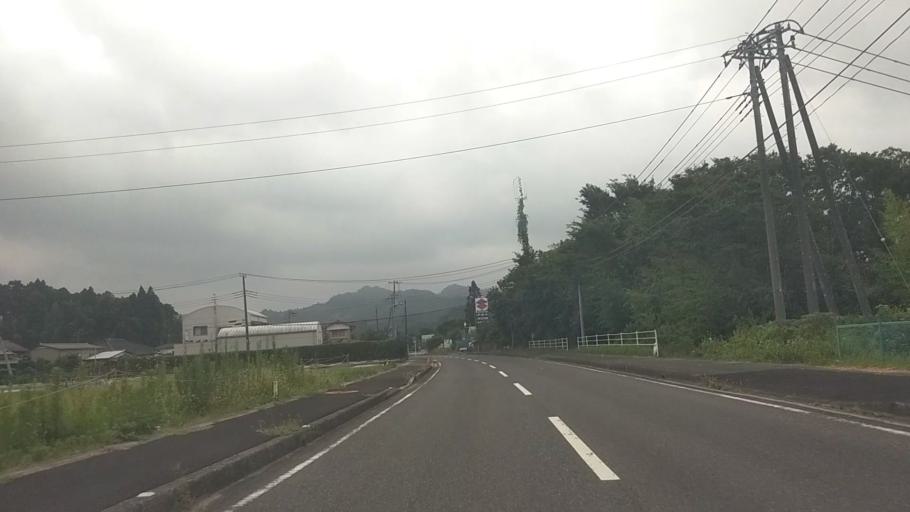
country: JP
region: Chiba
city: Kawaguchi
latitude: 35.2331
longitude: 140.0868
